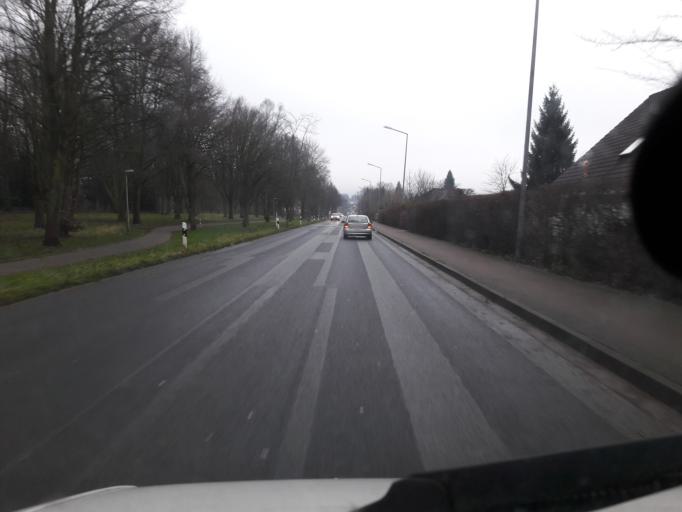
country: DE
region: North Rhine-Westphalia
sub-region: Regierungsbezirk Detmold
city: Minden
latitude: 52.2777
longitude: 8.8880
